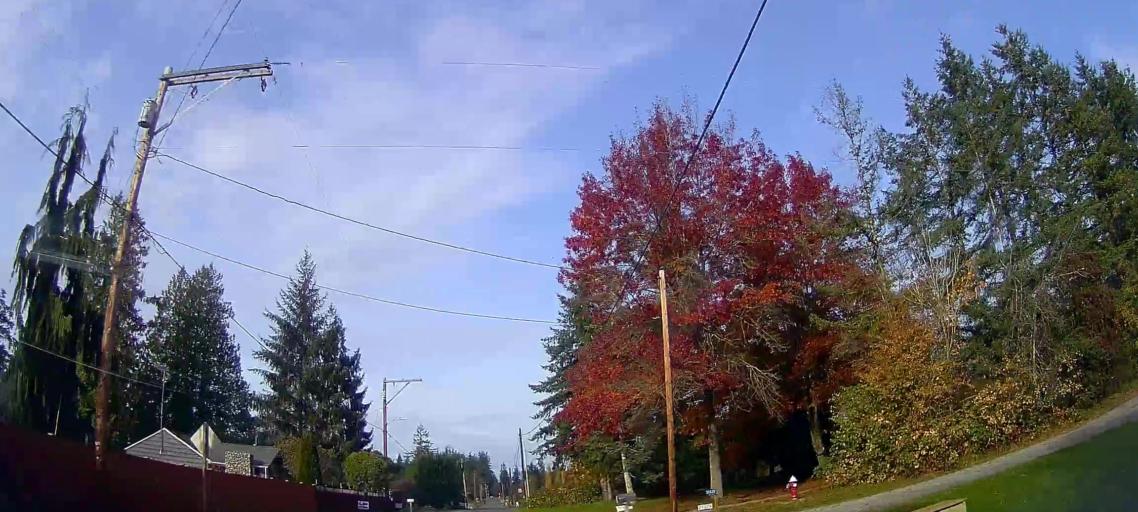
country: US
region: Washington
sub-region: Snohomish County
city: Stanwood
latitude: 48.2498
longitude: -122.3413
